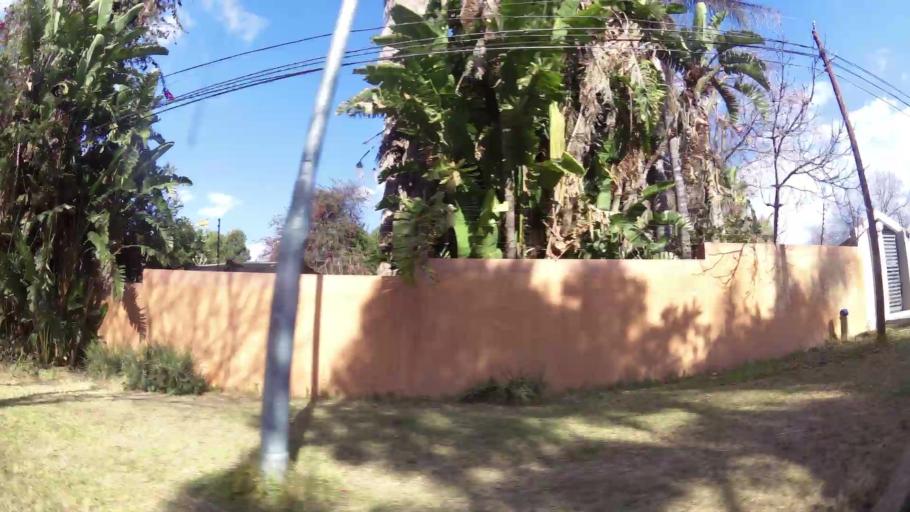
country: ZA
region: Gauteng
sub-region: City of Johannesburg Metropolitan Municipality
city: Diepsloot
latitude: -26.0213
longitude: 28.0263
